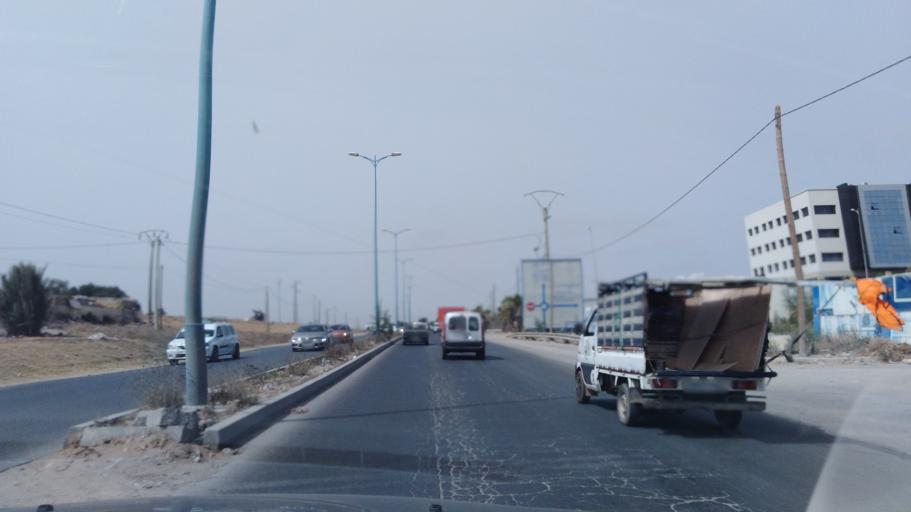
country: MA
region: Grand Casablanca
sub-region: Nouaceur
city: Bouskoura
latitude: 33.5187
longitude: -7.6937
